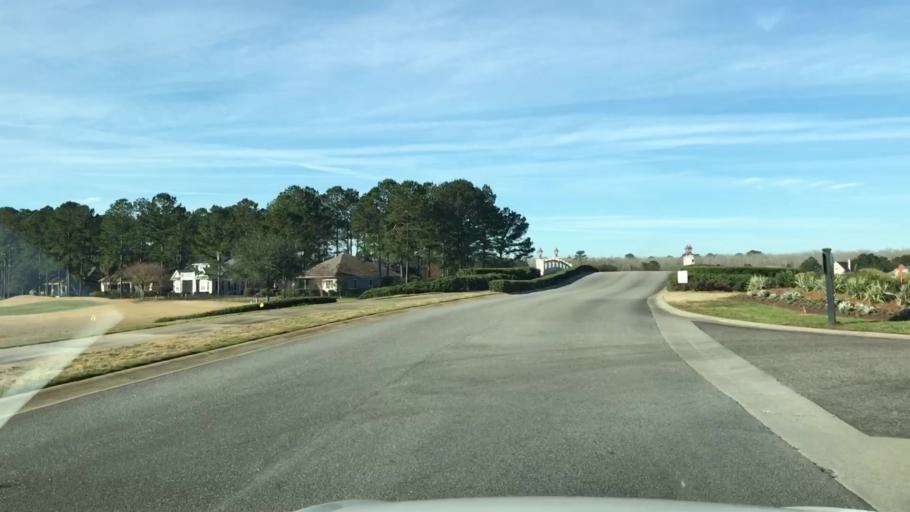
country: US
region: South Carolina
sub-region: Beaufort County
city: Bluffton
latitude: 32.2558
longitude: -80.9056
